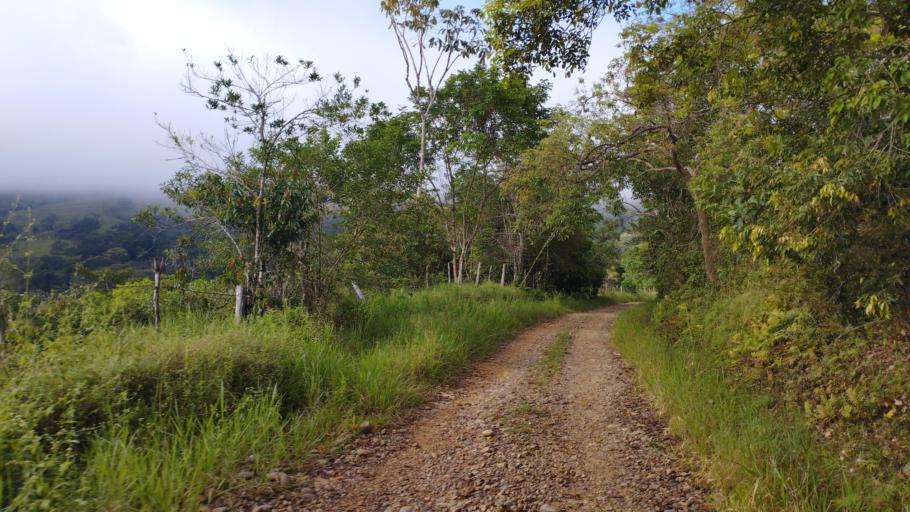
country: CO
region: Casanare
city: Sabanalarga
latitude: 4.7627
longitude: -73.0798
